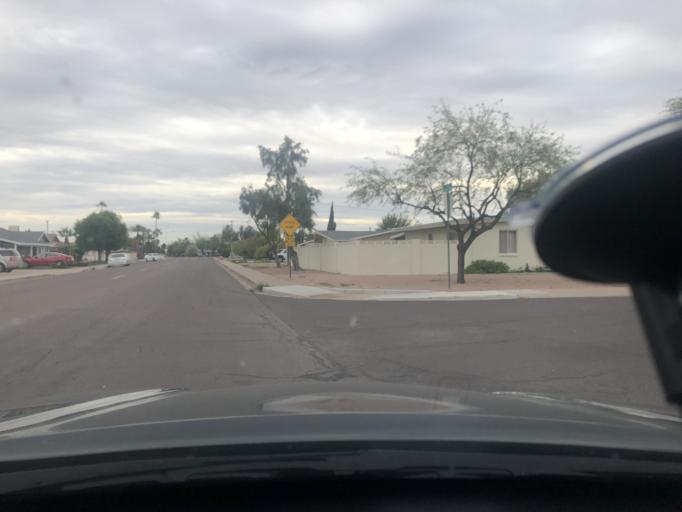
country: US
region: Arizona
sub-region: Maricopa County
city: Scottsdale
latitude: 33.4851
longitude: -111.9003
